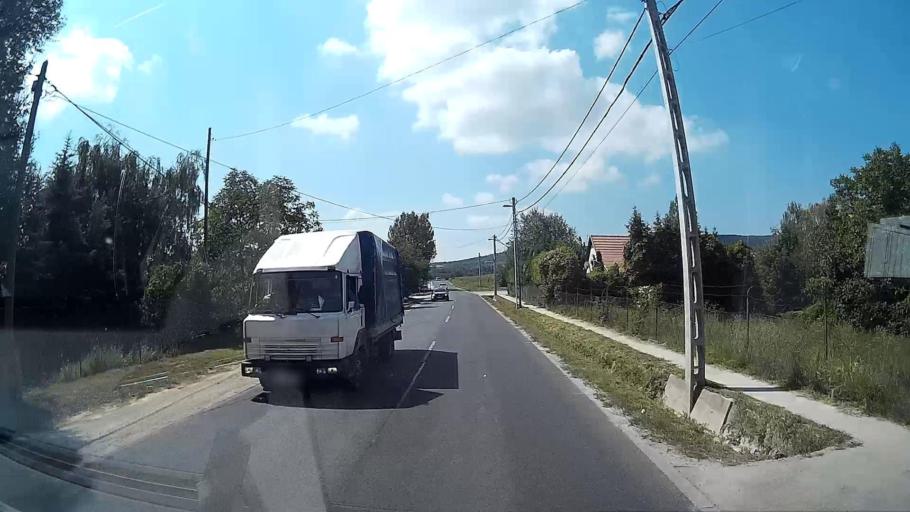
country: HU
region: Pest
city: Budakalasz
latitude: 47.6155
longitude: 19.0333
